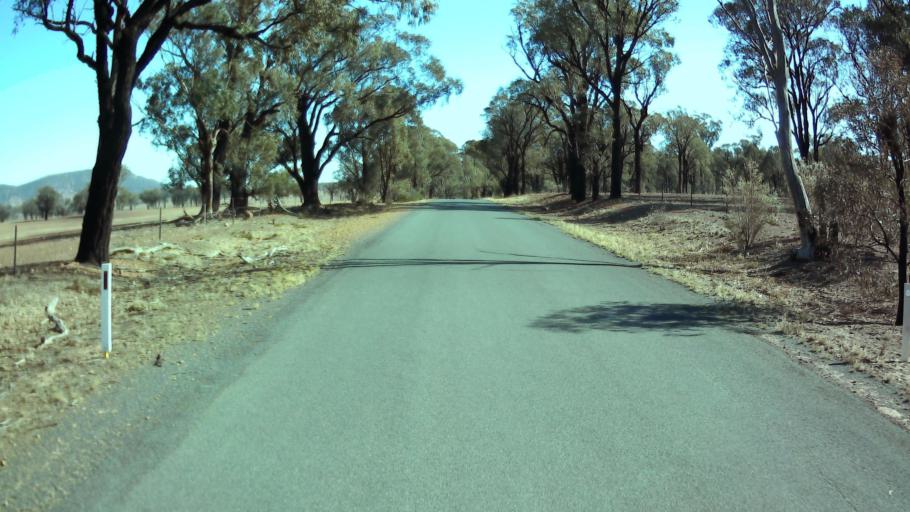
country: AU
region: New South Wales
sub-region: Weddin
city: Grenfell
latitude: -33.7869
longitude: 147.9581
